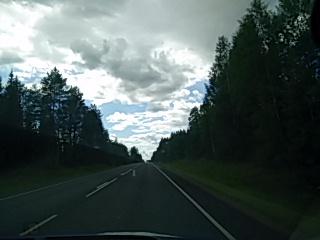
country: FI
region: Haeme
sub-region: Haemeenlinna
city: Renko
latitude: 60.8658
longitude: 24.1950
